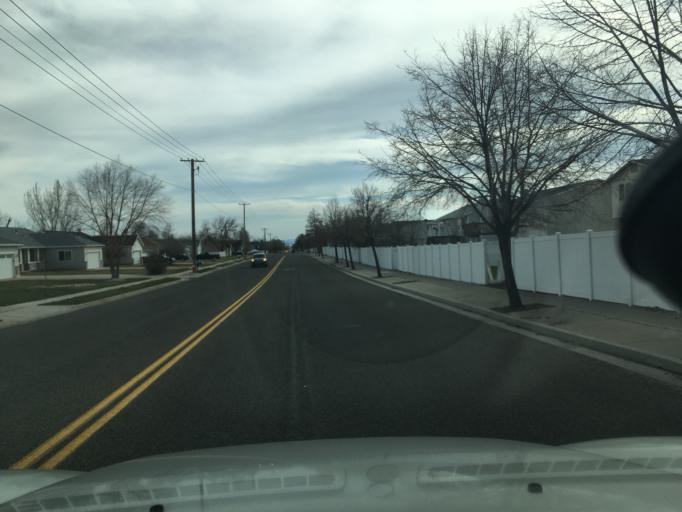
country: US
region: Utah
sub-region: Davis County
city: Clearfield
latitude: 41.0806
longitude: -112.0070
